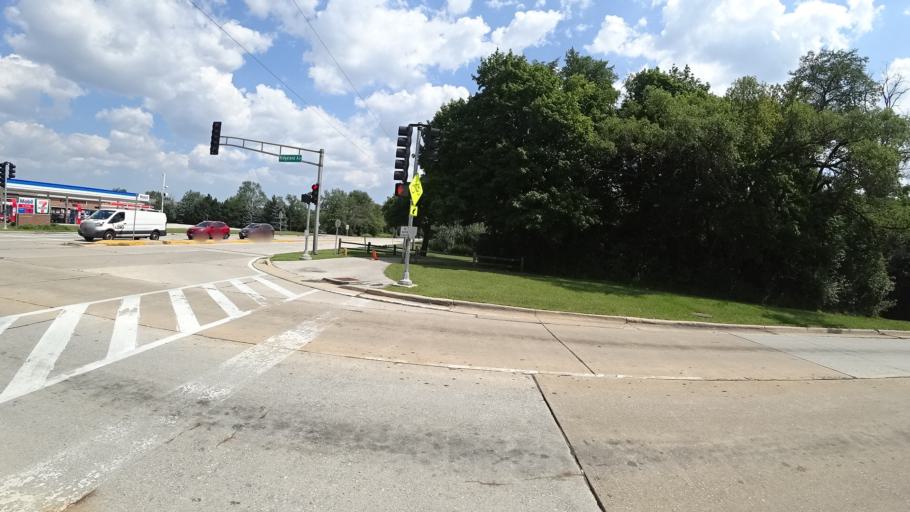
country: US
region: Illinois
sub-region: Cook County
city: Crestwood
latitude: 41.6463
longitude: -87.7770
